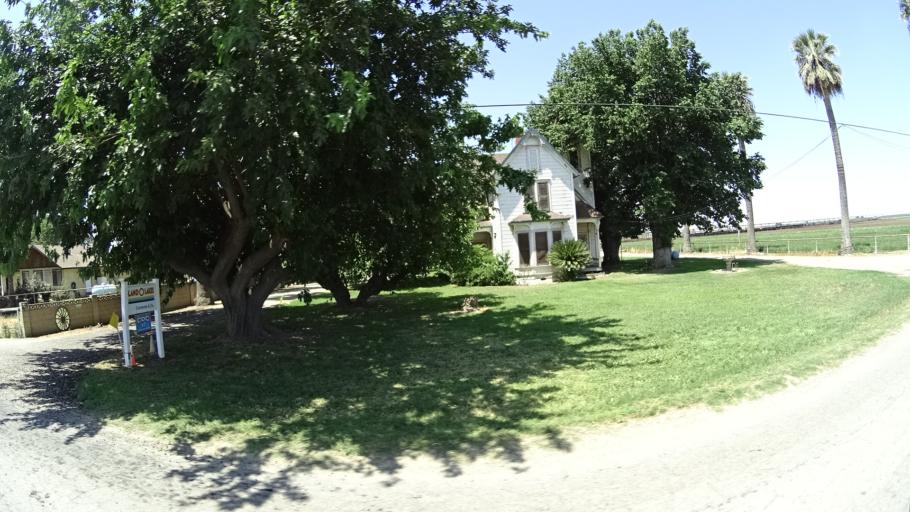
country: US
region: California
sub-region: Kings County
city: Armona
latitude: 36.3587
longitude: -119.7269
